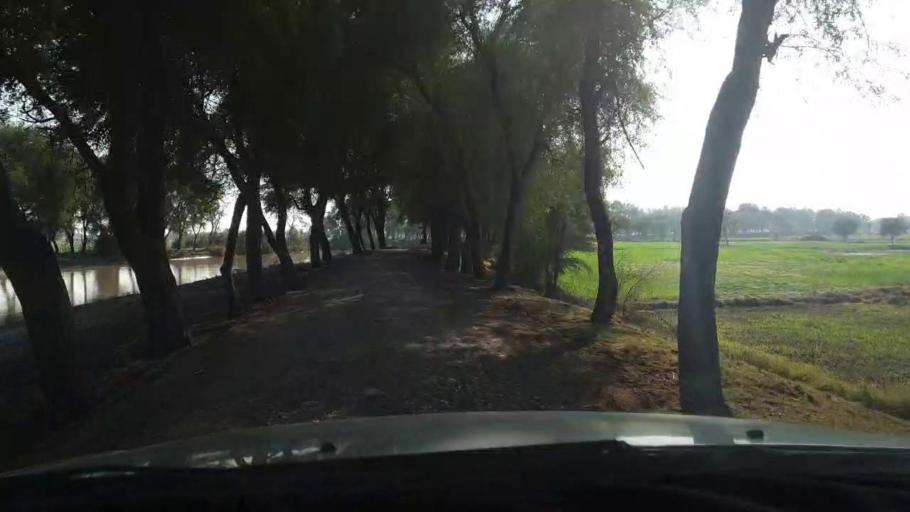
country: PK
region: Sindh
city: Mirpur Mathelo
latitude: 27.9860
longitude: 69.5448
